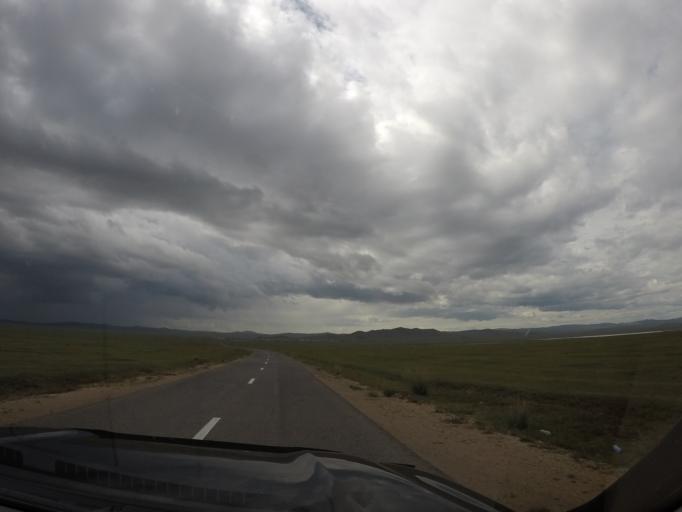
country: MN
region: Hentiy
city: Avraga
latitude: 47.4798
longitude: 109.5134
